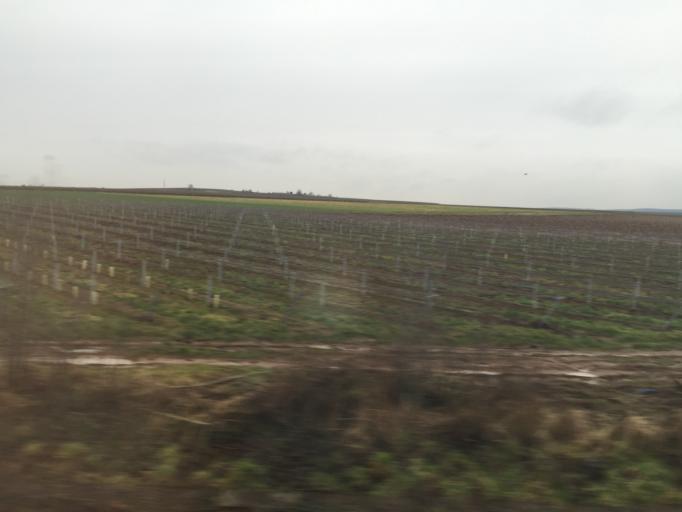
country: DE
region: Baden-Wuerttemberg
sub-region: Regierungsbezirk Stuttgart
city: Talheim
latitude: 49.0839
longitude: 9.1731
